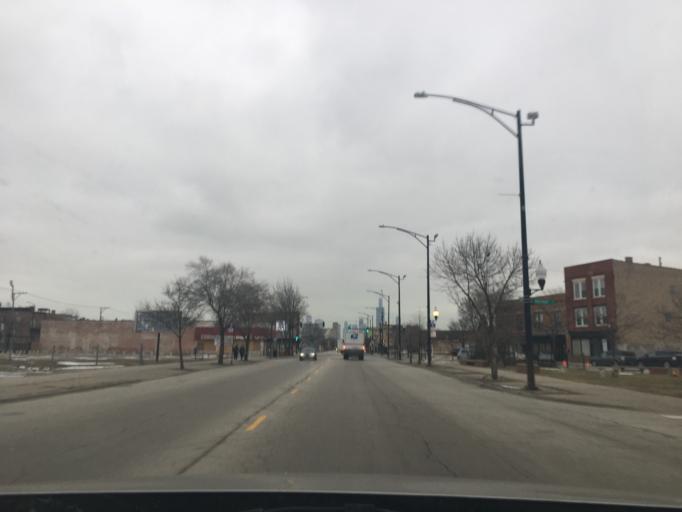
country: US
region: Illinois
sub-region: Cook County
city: Chicago
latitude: 41.8811
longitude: -87.6979
